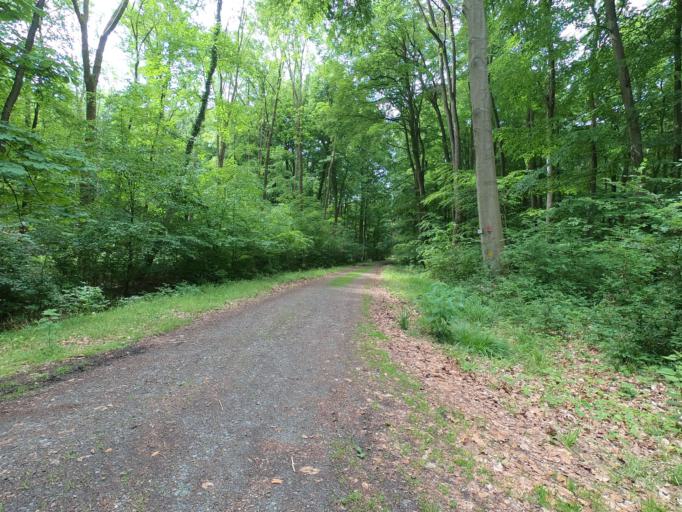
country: DE
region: Hesse
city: Morfelden-Walldorf
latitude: 49.9776
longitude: 8.5347
